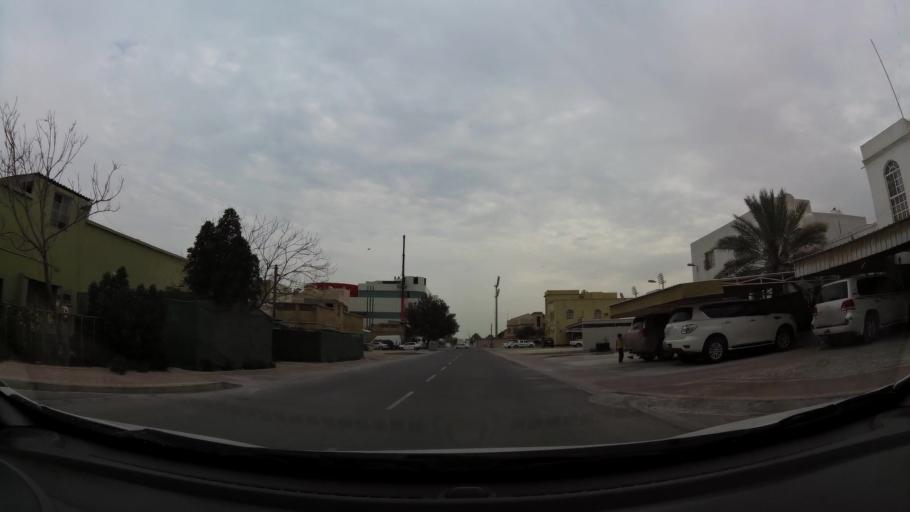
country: BH
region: Northern
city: Ar Rifa'
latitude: 26.0586
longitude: 50.6168
